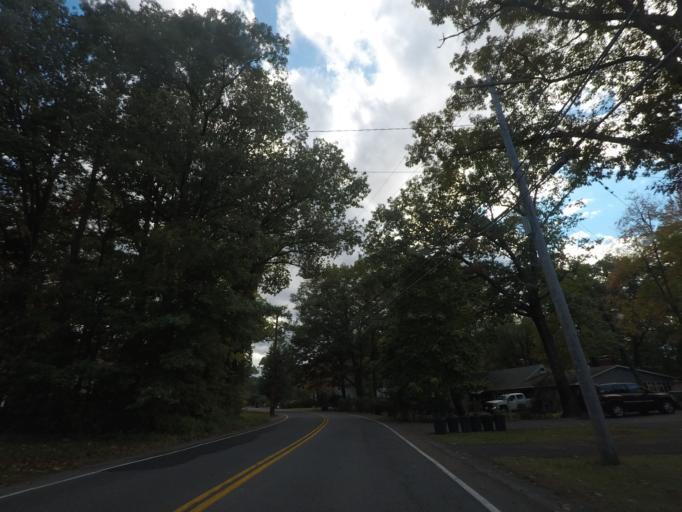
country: US
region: New York
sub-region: Albany County
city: Colonie
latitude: 42.7415
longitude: -73.8372
